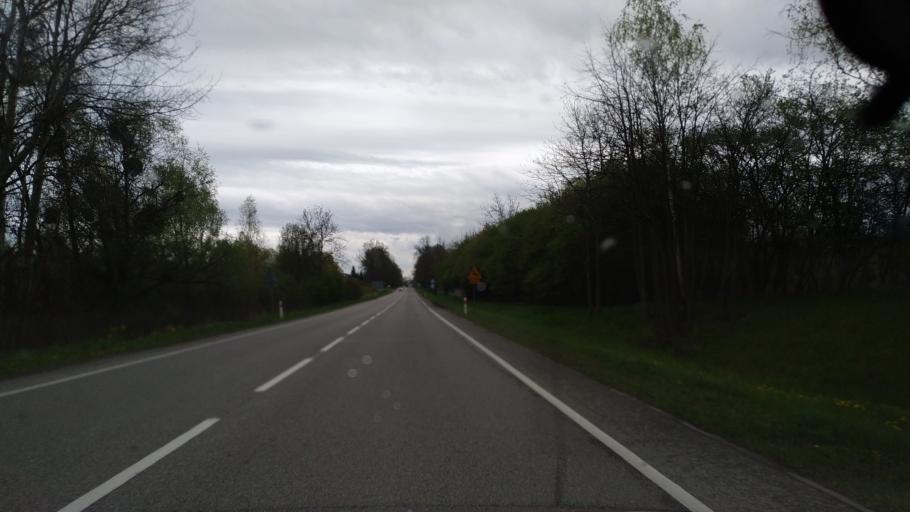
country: PL
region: Pomeranian Voivodeship
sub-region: Powiat starogardzki
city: Starogard Gdanski
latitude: 53.9985
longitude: 18.5910
